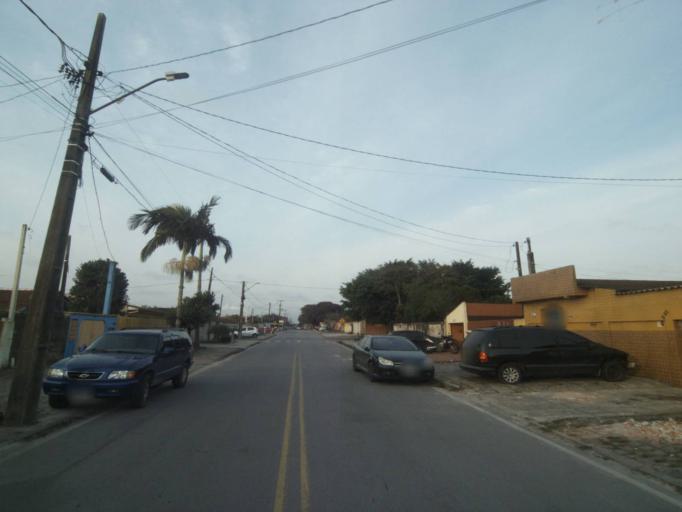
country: BR
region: Parana
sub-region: Paranagua
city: Paranagua
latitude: -25.5159
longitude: -48.5452
